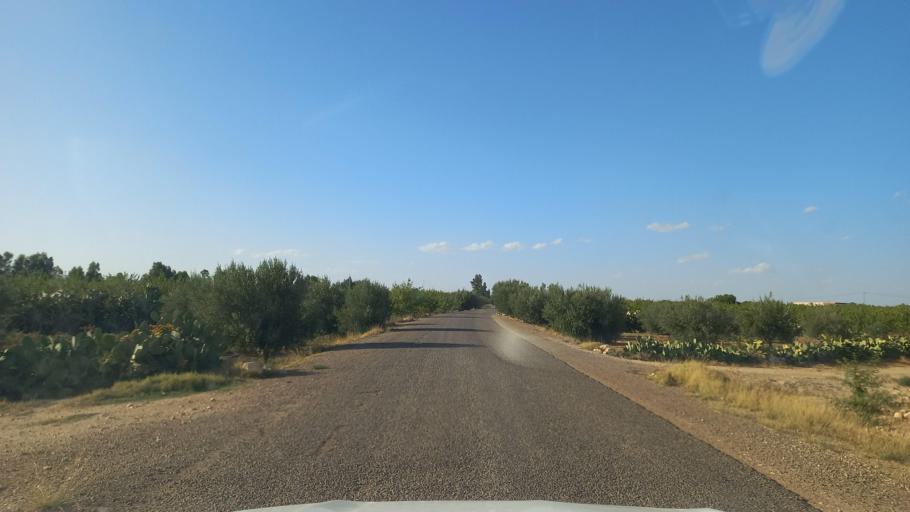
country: TN
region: Al Qasrayn
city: Kasserine
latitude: 35.2632
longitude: 9.0284
